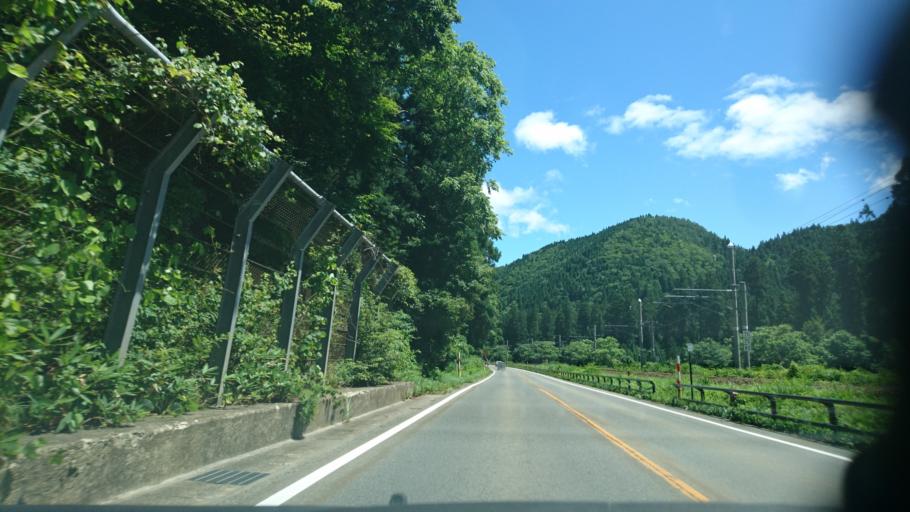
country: JP
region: Akita
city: Kakunodatemachi
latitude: 39.6438
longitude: 140.6622
